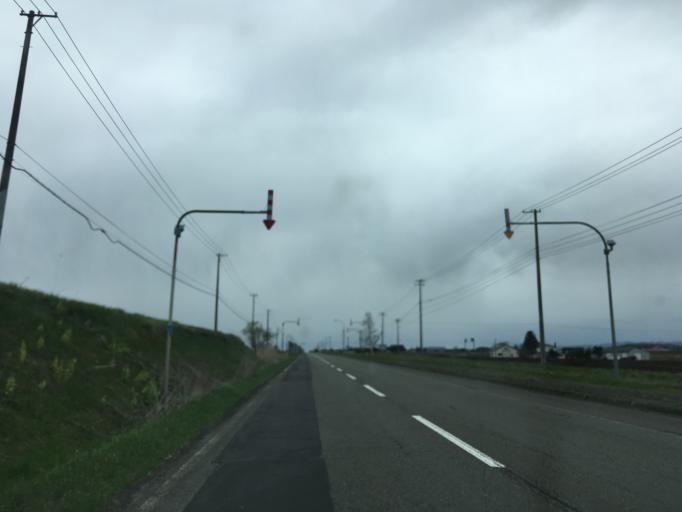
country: JP
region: Hokkaido
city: Chitose
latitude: 42.9240
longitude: 141.8083
